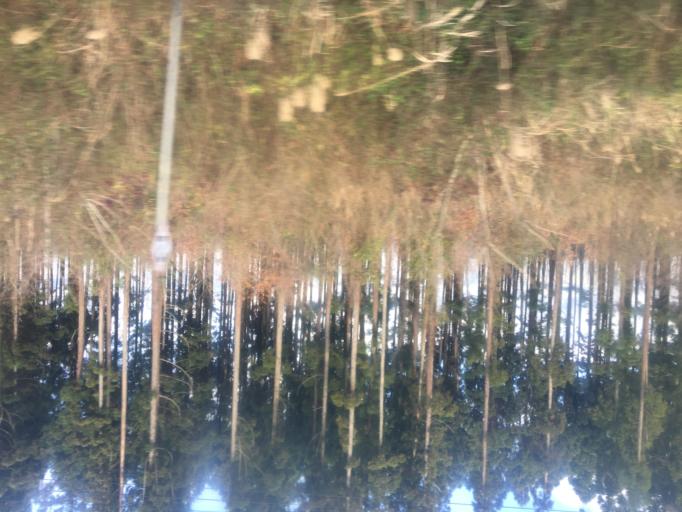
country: JP
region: Akita
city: Noshiromachi
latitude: 40.1939
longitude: 140.0722
